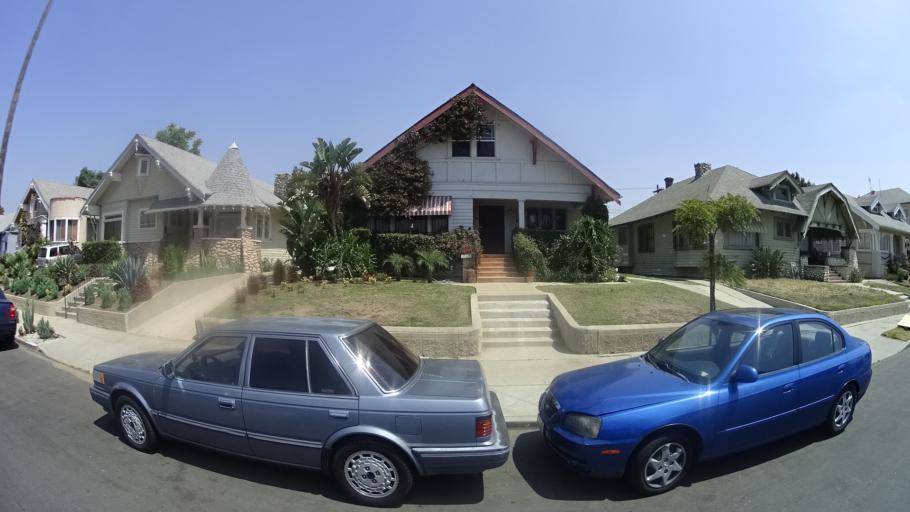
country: US
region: California
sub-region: Los Angeles County
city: View Park-Windsor Hills
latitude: 34.0300
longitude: -118.3103
